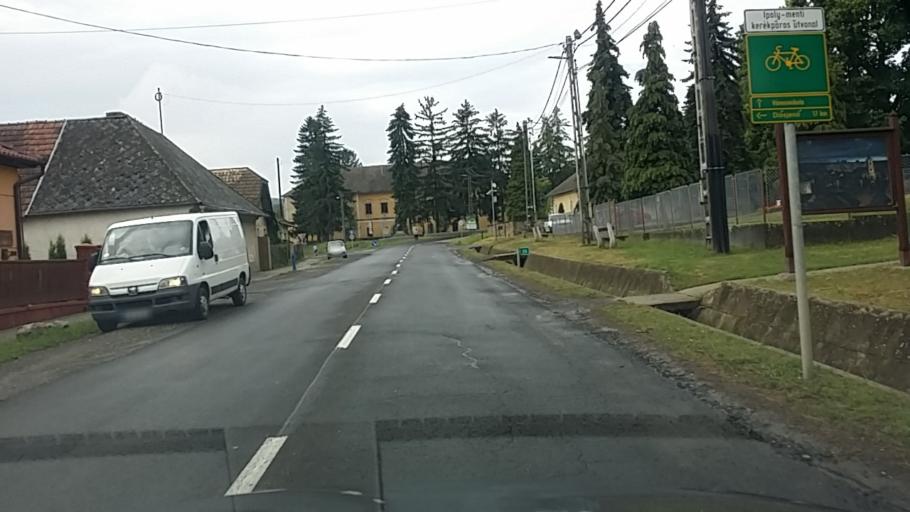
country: SK
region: Nitriansky
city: Sahy
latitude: 48.0192
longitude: 18.8931
